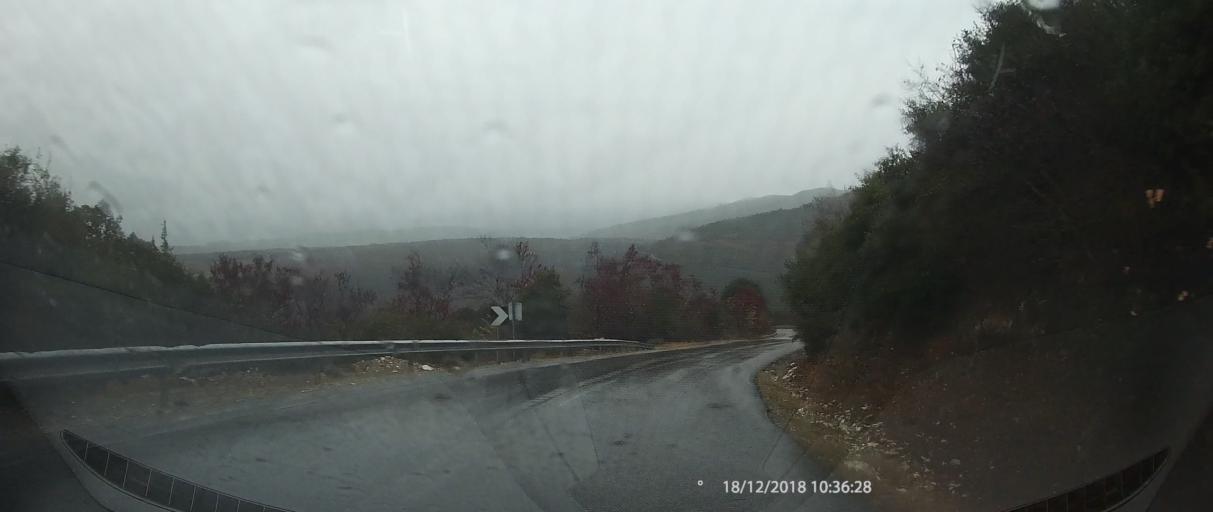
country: GR
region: Central Macedonia
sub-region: Nomos Pierias
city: Kato Milia
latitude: 40.2160
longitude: 22.3107
